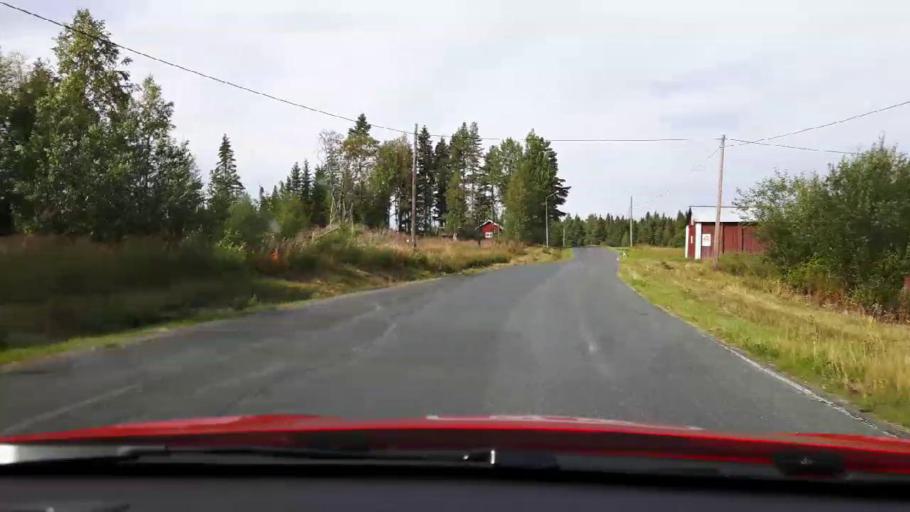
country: SE
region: Jaemtland
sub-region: Krokoms Kommun
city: Valla
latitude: 63.2745
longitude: 13.8799
